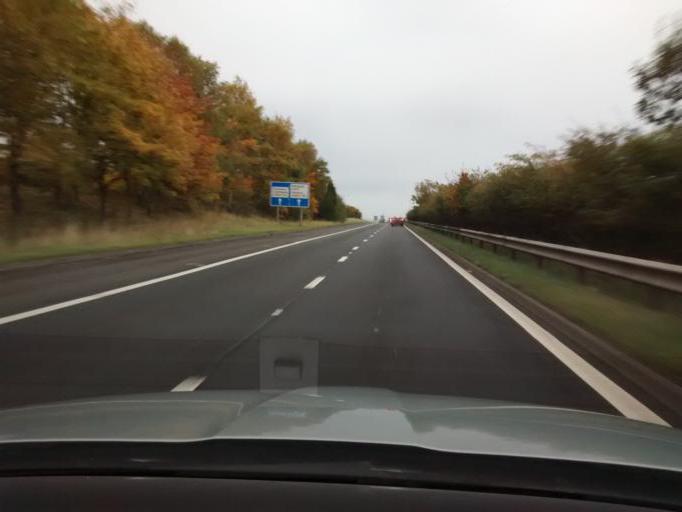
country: GB
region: Scotland
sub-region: Falkirk
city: Polmont
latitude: 55.9894
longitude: -3.6878
